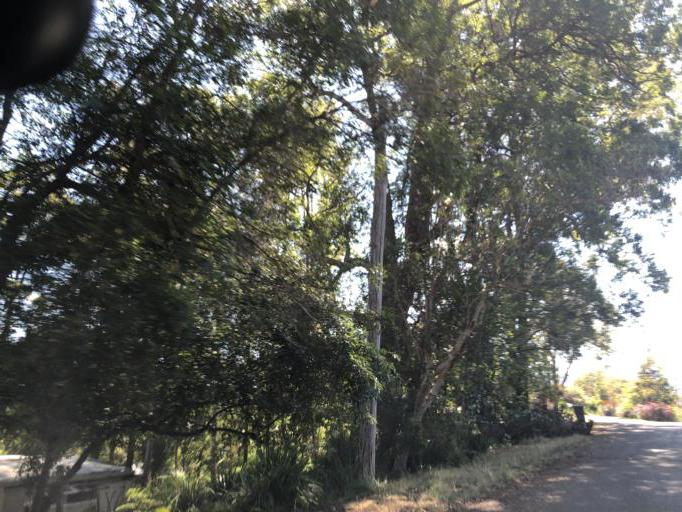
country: AU
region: New South Wales
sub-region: Bellingen
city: Bellingen
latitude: -30.4605
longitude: 152.8974
